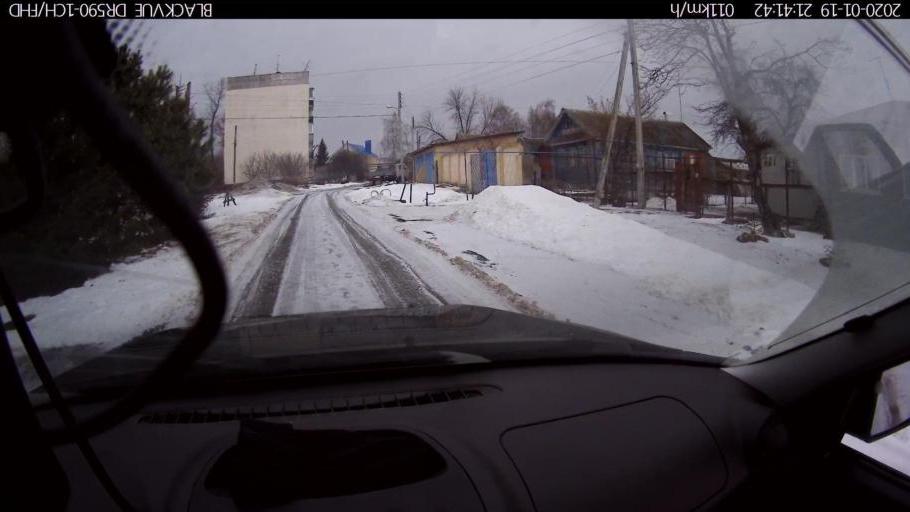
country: RU
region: Nizjnij Novgorod
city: Nizhniy Novgorod
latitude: 56.2330
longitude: 43.9782
